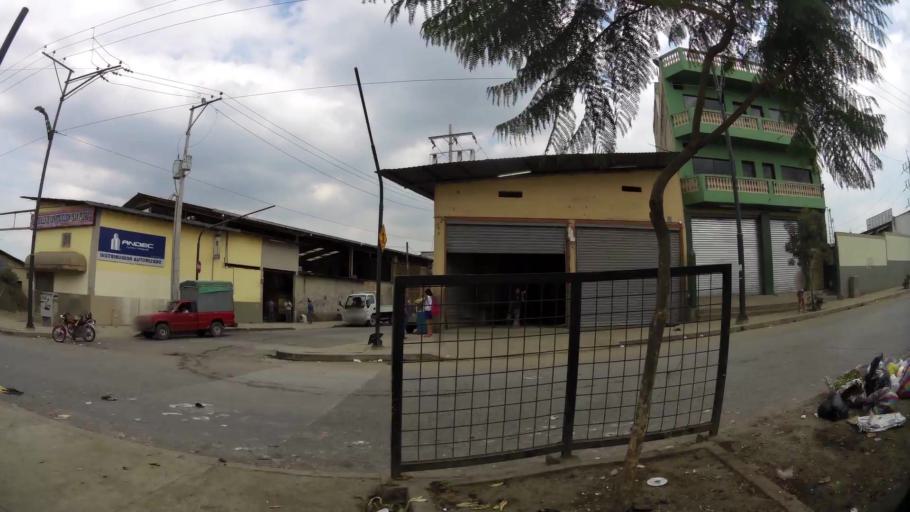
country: EC
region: Guayas
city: Santa Lucia
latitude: -2.1063
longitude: -79.9585
